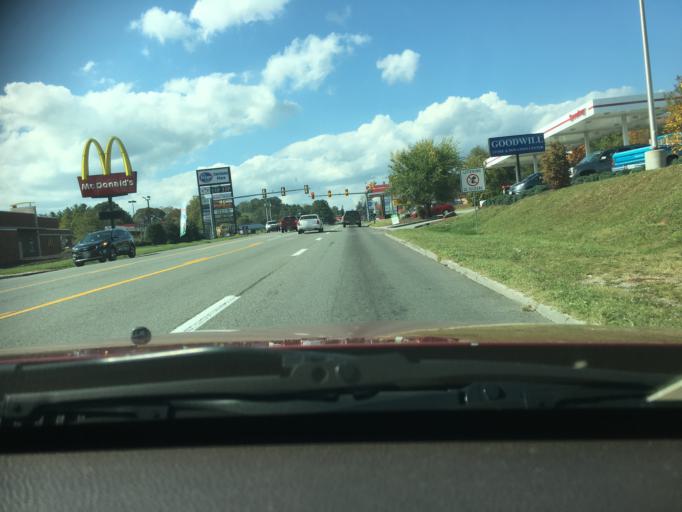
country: US
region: Virginia
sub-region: Pulaski County
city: Fairlawn
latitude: 37.1421
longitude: -80.5789
